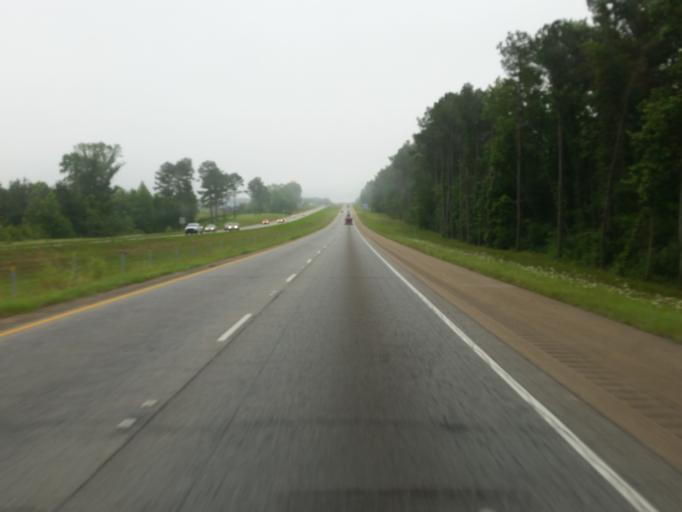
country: US
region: Louisiana
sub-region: Webster Parish
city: Minden
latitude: 32.5832
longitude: -93.2617
